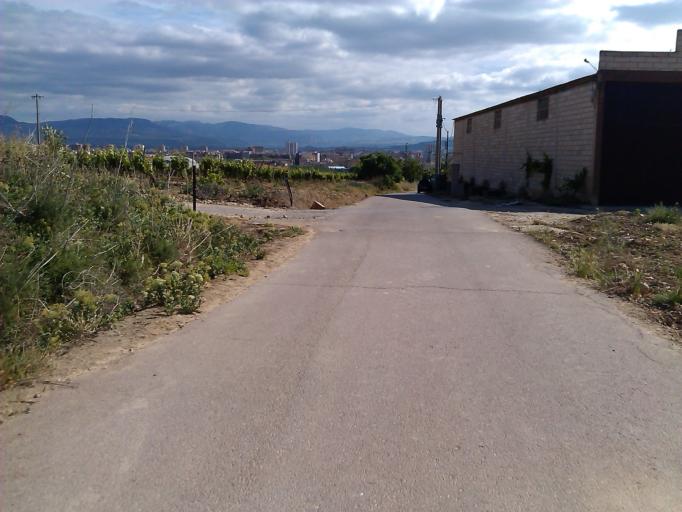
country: ES
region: La Rioja
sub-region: Provincia de La Rioja
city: Logrono
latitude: 42.4799
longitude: -2.4357
